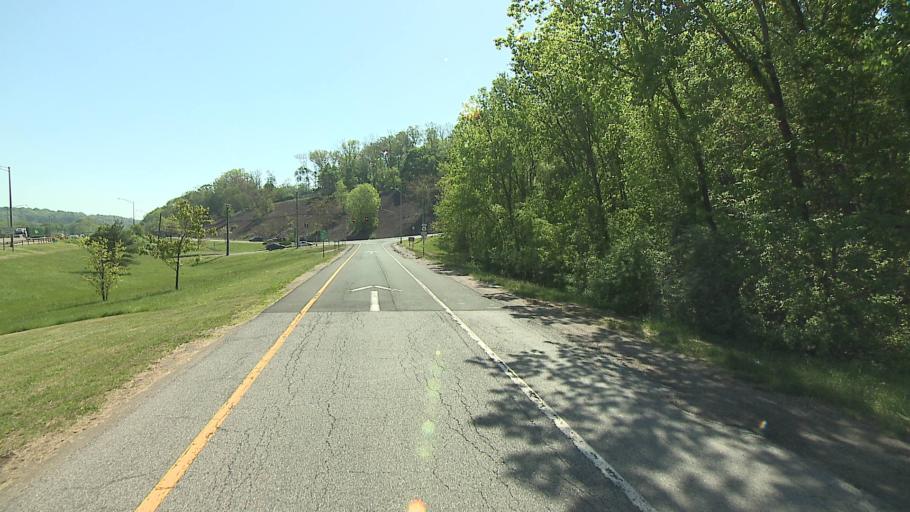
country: US
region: New York
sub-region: Putnam County
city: Peach Lake
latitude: 41.3889
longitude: -73.5416
